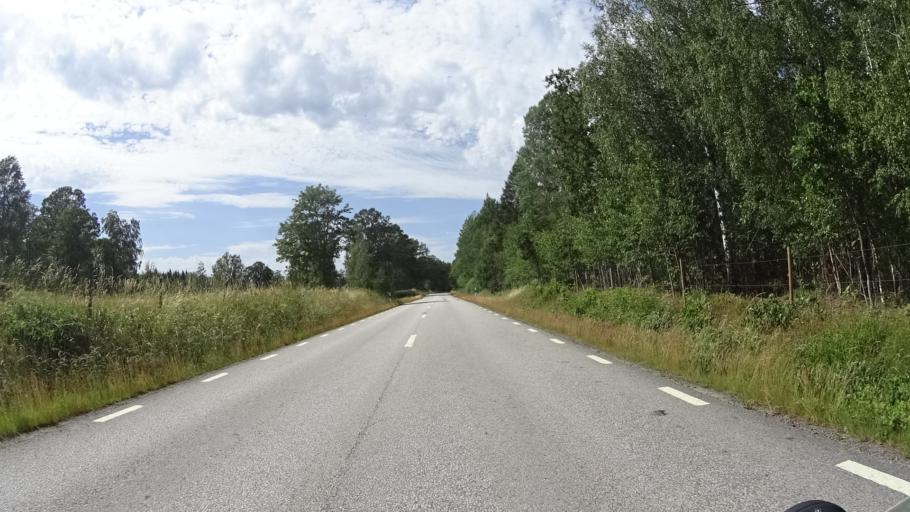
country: SE
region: OEstergoetland
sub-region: Atvidabergs Kommun
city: Atvidaberg
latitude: 58.0928
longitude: 16.1311
